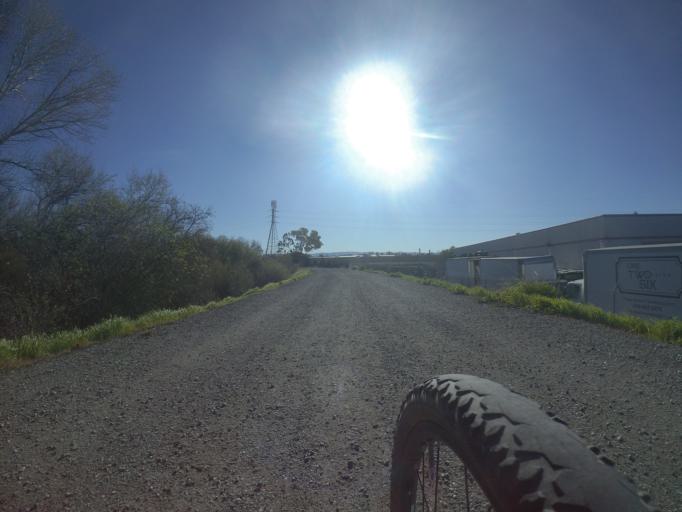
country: US
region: California
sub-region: Santa Clara County
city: Santa Clara
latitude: 37.3827
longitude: -121.9382
